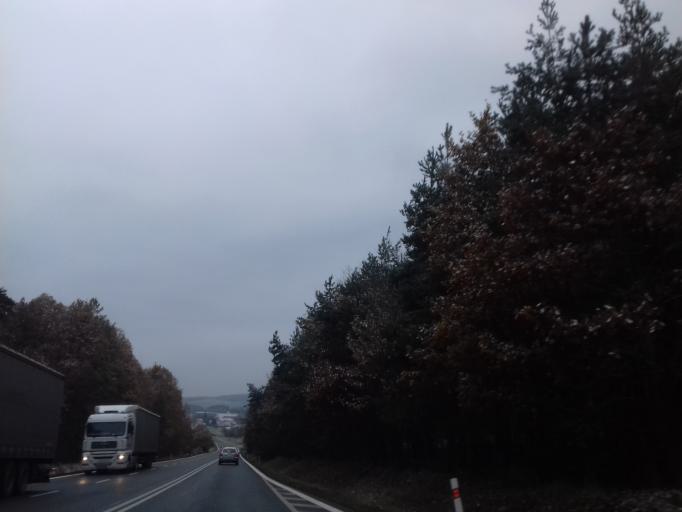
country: CZ
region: Plzensky
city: Holysov
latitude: 49.6047
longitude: 13.1164
